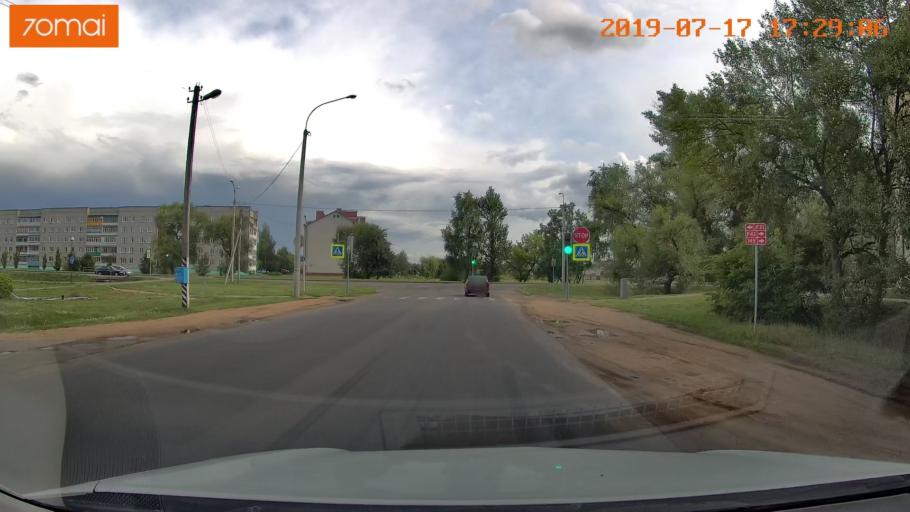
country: BY
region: Mogilev
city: Babruysk
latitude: 53.1238
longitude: 29.1663
